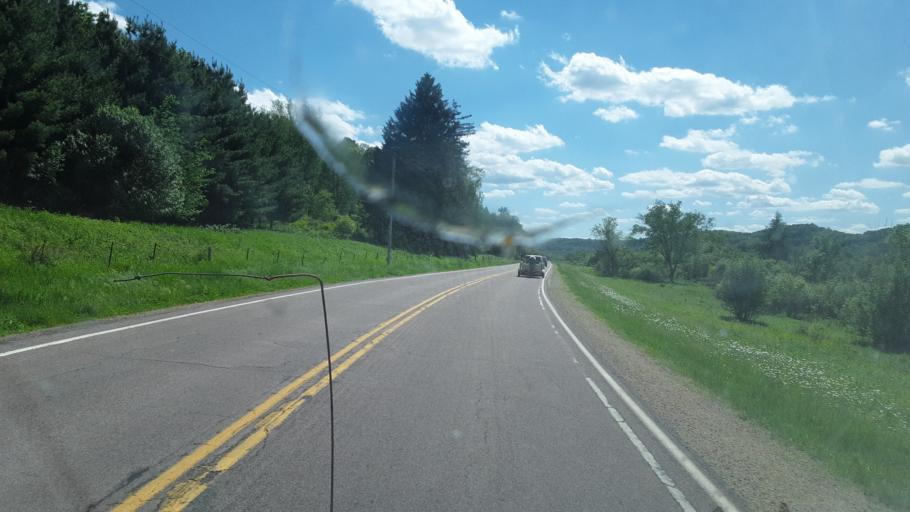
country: US
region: Wisconsin
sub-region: Richland County
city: Richland Center
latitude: 43.3903
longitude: -90.2420
